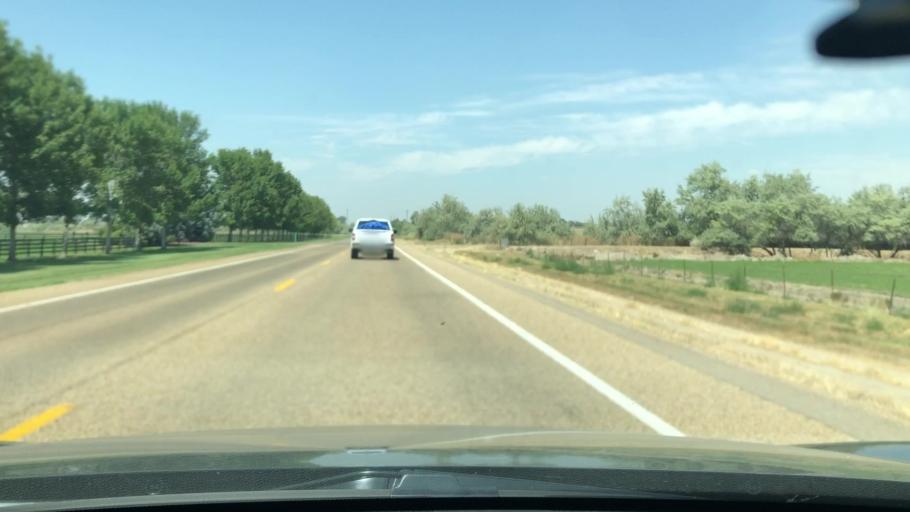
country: US
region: Idaho
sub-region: Canyon County
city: Parma
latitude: 43.7586
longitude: -116.9117
